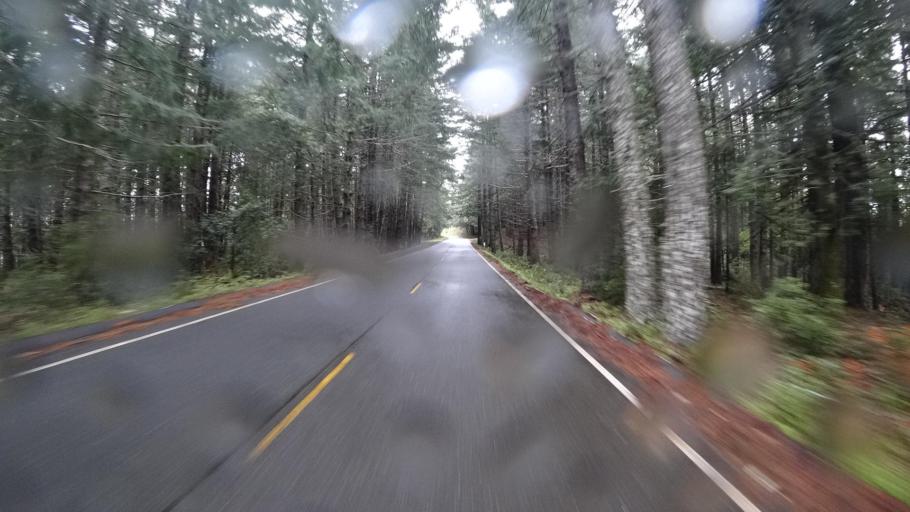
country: US
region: California
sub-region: Humboldt County
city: Westhaven-Moonstone
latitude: 41.1970
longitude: -123.9419
